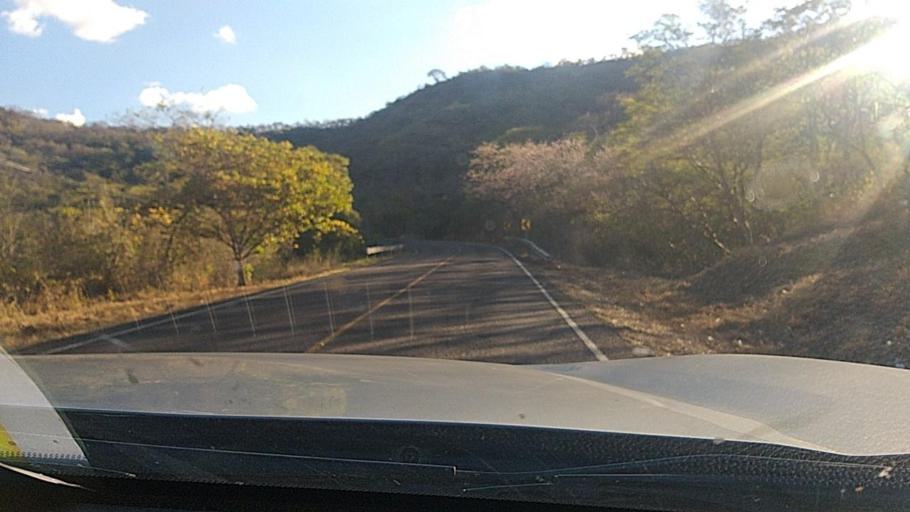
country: NI
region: Esteli
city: Condega
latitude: 13.2610
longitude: -86.3544
